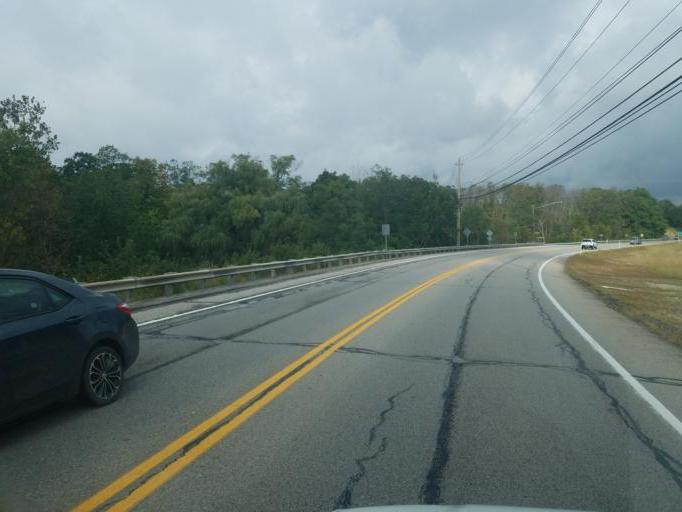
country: US
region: Ohio
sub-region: Geauga County
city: Chardon
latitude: 41.5923
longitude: -81.2275
